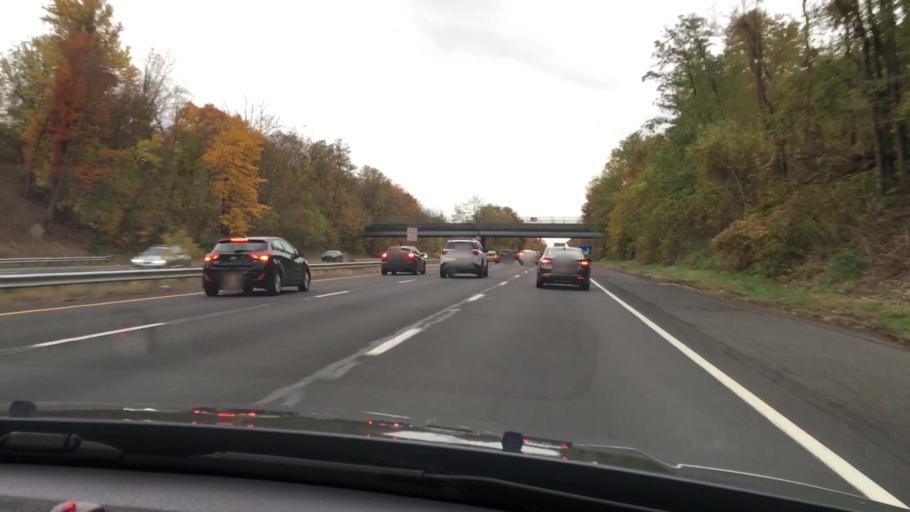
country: US
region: New Jersey
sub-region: Somerset County
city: Bernardsville
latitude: 40.7134
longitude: -74.5561
